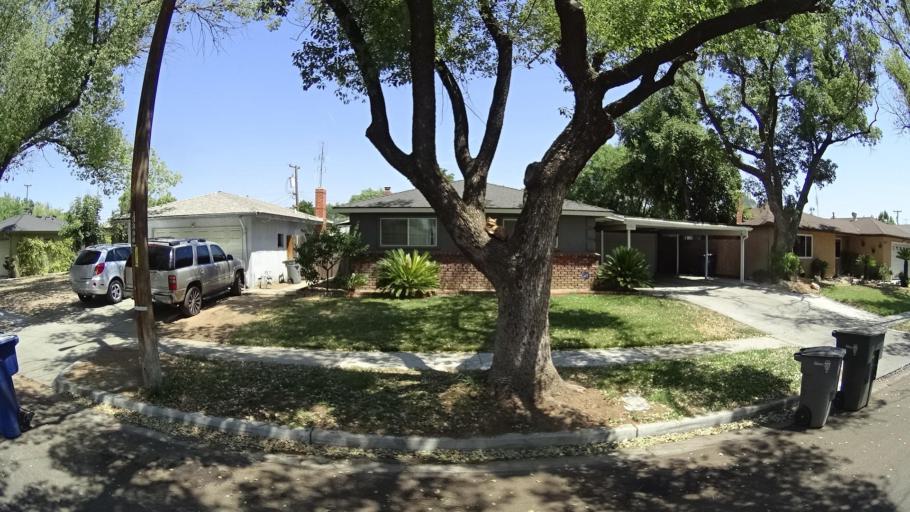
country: US
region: California
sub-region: Fresno County
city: Sunnyside
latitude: 36.7636
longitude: -119.7288
